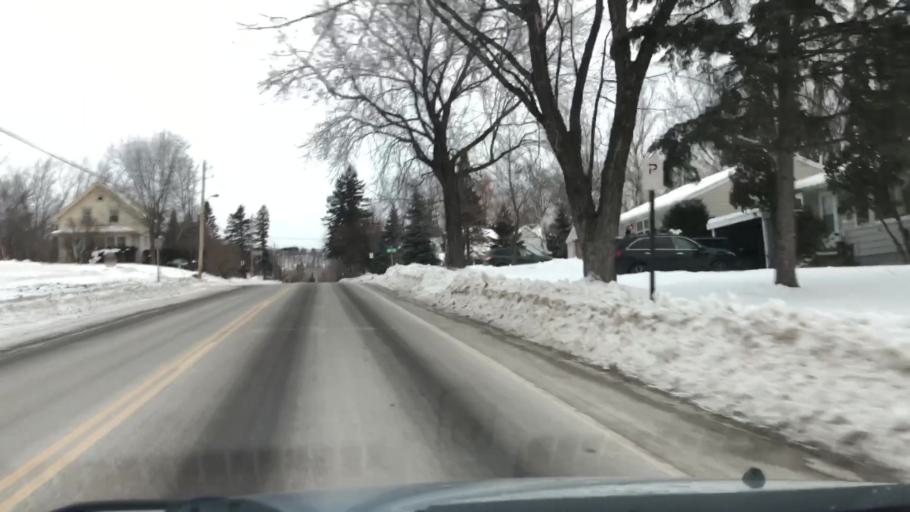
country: US
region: Minnesota
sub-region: Saint Louis County
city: Arnold
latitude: 46.8328
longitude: -92.0368
